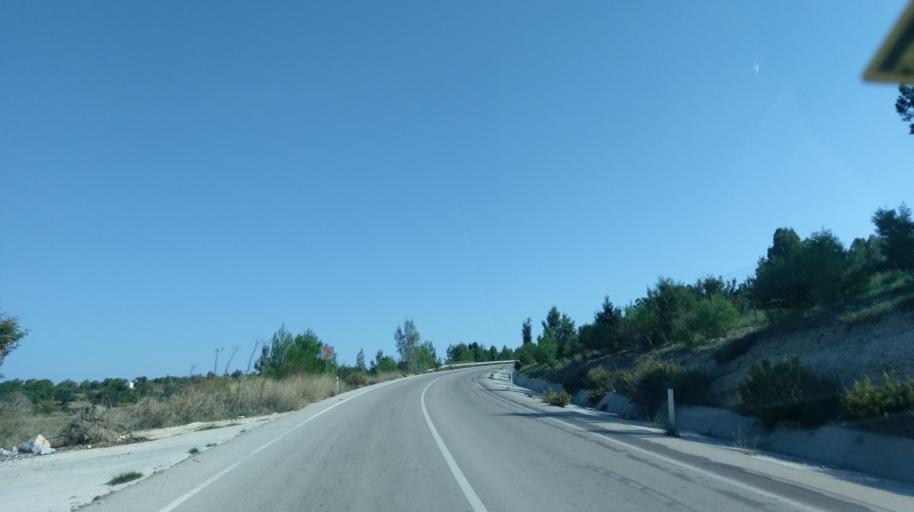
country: CY
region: Ammochostos
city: Trikomo
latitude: 35.4290
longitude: 33.9724
